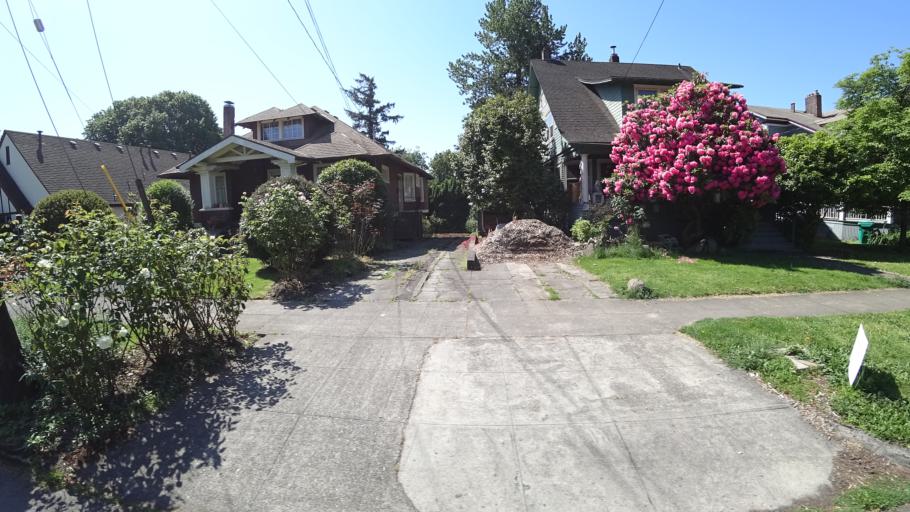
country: US
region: Oregon
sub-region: Multnomah County
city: Portland
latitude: 45.5314
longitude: -122.6432
